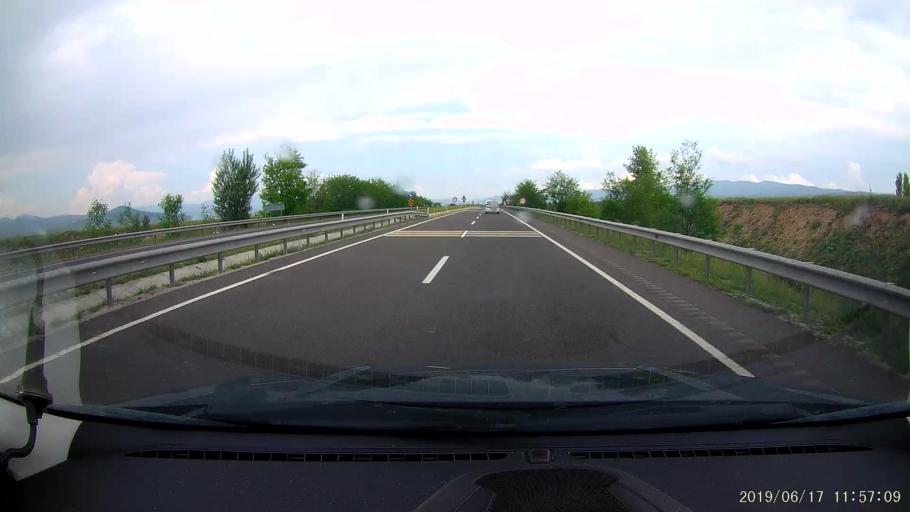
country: TR
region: Cankiri
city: Cerkes
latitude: 40.8060
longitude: 32.9640
